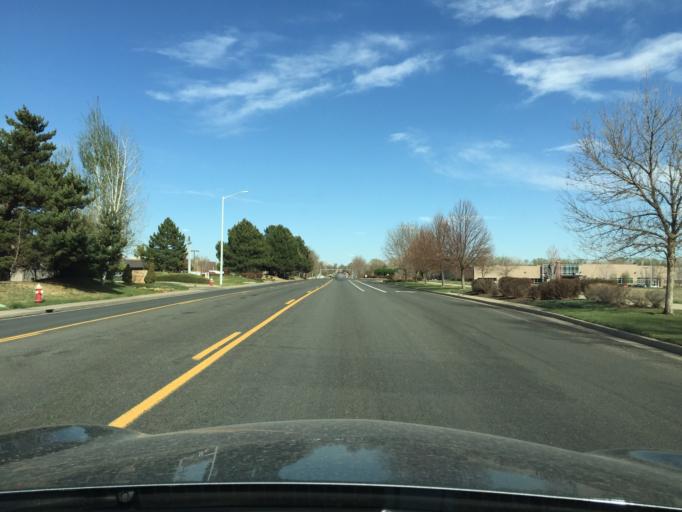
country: US
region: Colorado
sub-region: Boulder County
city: Longmont
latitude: 40.1379
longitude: -105.1266
